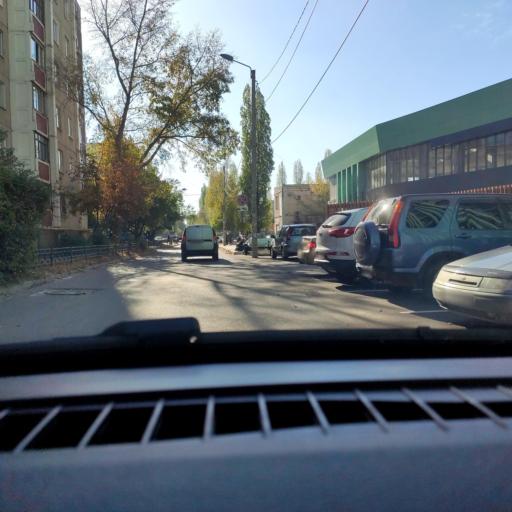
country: RU
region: Voronezj
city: Podgornoye
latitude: 51.7178
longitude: 39.1669
